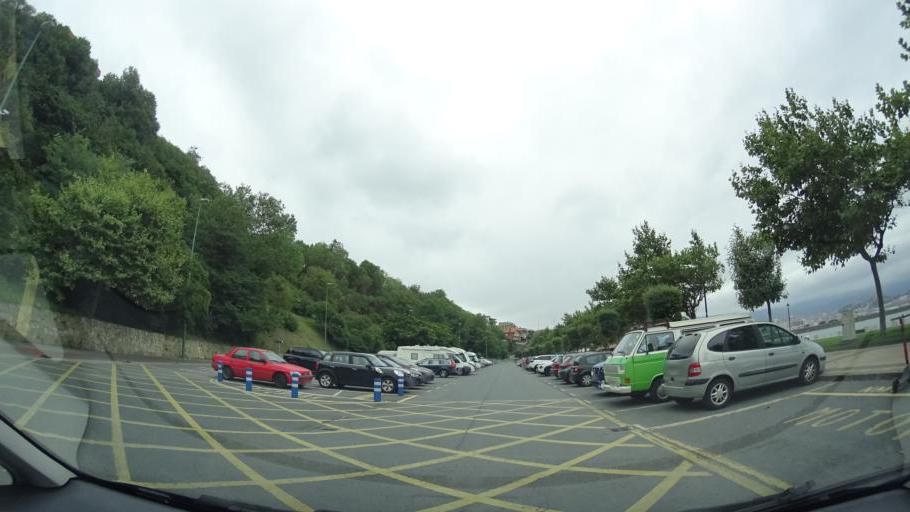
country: ES
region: Basque Country
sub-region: Bizkaia
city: Algorta
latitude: 43.3466
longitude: -3.0116
